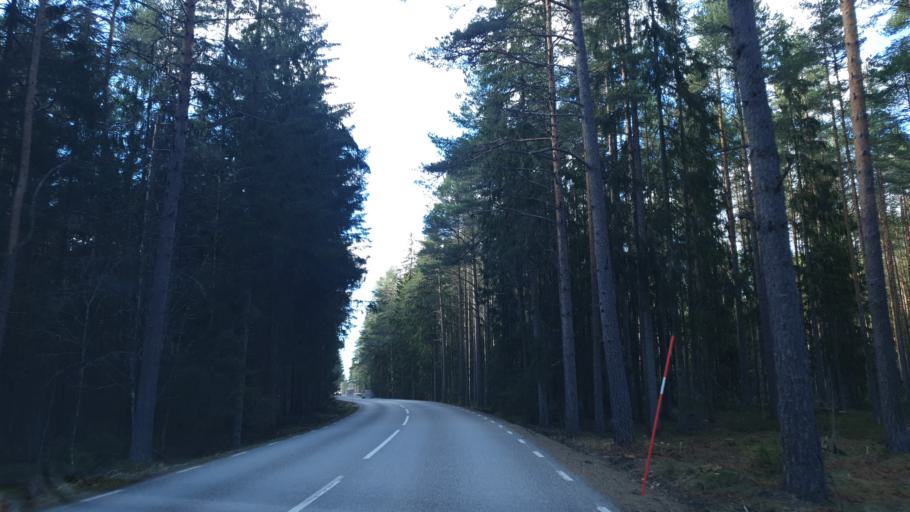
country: SE
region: OErebro
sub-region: Orebro Kommun
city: Hovsta
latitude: 59.3312
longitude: 15.1083
